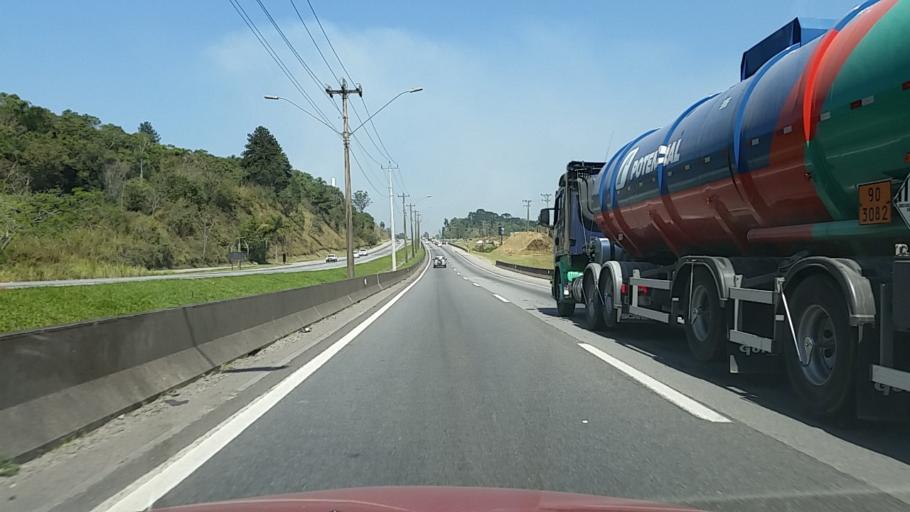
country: BR
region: Sao Paulo
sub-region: Itapecerica Da Serra
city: Itapecerica da Serra
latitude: -23.7258
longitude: -46.8932
